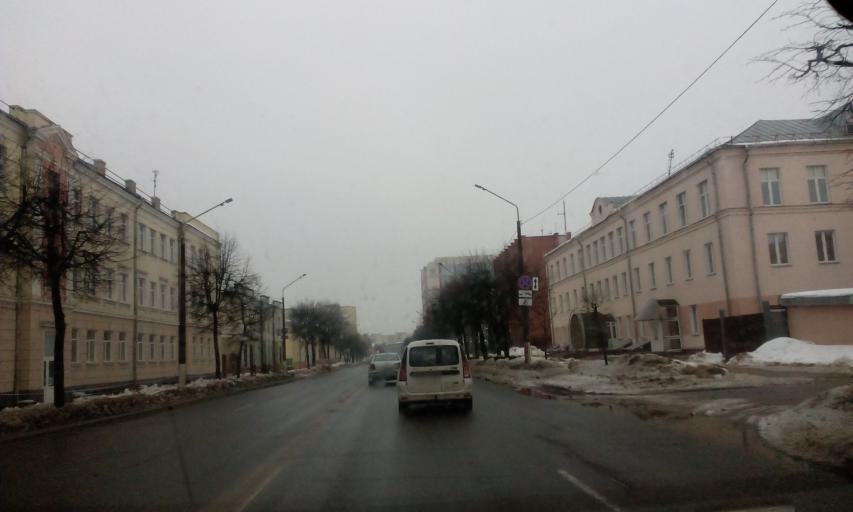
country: BY
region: Mogilev
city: Mahilyow
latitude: 53.8986
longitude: 30.3399
